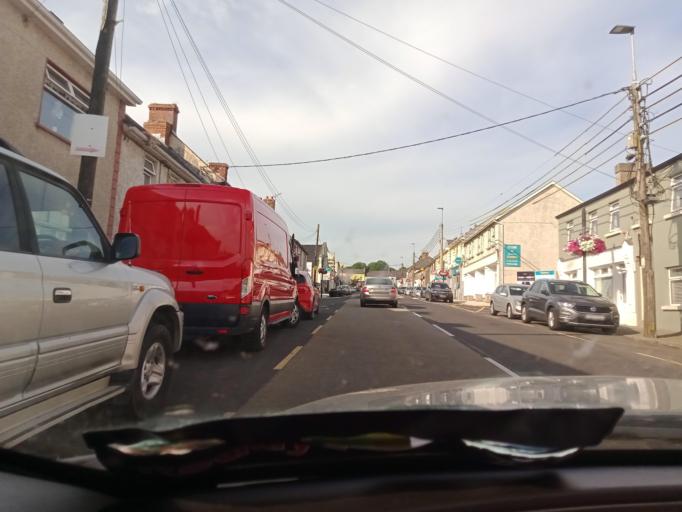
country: IE
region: Ulster
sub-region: An Cabhan
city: Cavan
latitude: 53.9305
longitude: -7.4100
